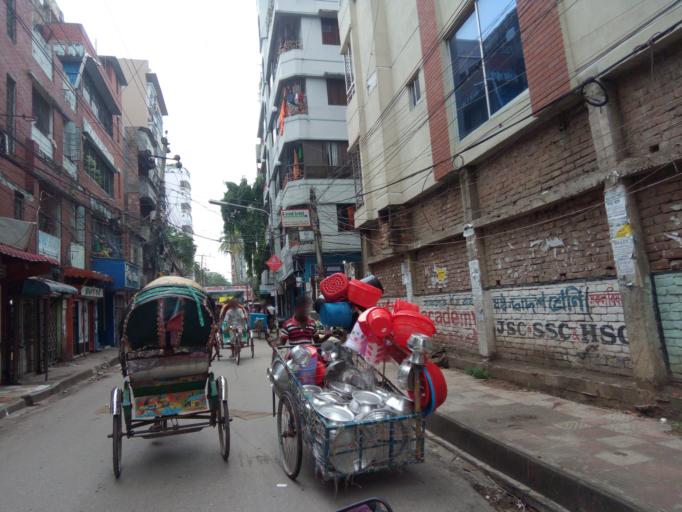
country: BD
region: Dhaka
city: Azimpur
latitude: 23.7577
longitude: 90.3674
